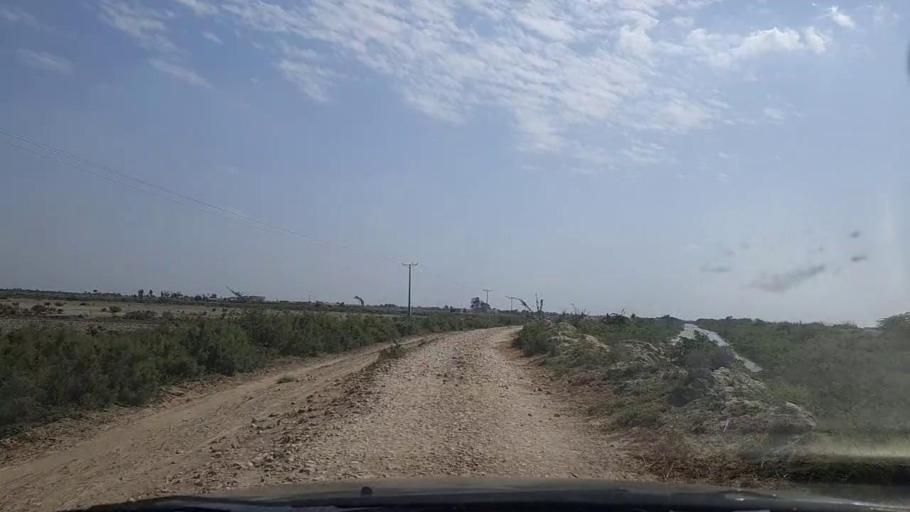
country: PK
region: Sindh
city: Mirpur Batoro
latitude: 24.5913
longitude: 68.1979
